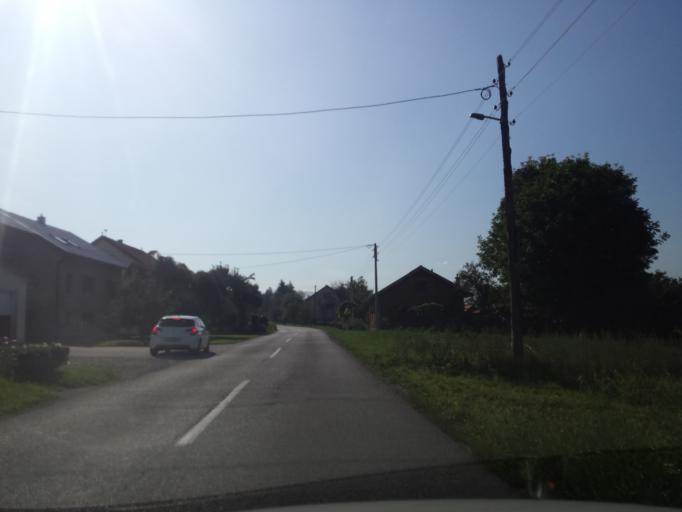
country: HR
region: Karlovacka
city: Ostarije
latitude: 45.2179
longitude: 15.2979
